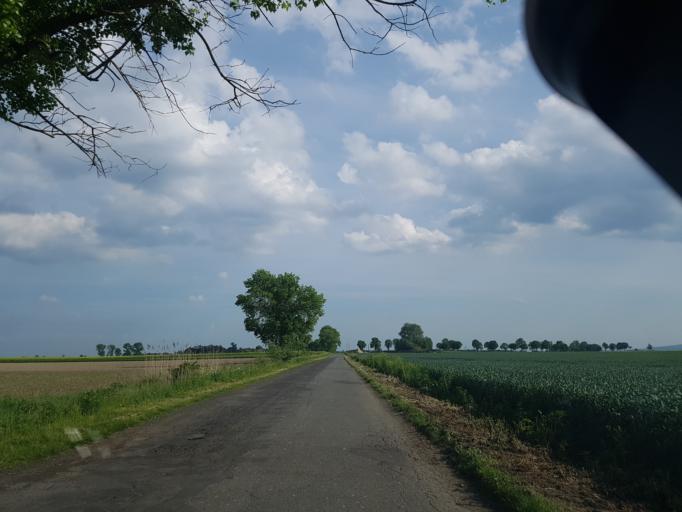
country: PL
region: Lower Silesian Voivodeship
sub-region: Powiat strzelinski
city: Wiazow
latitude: 50.8646
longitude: 17.1755
